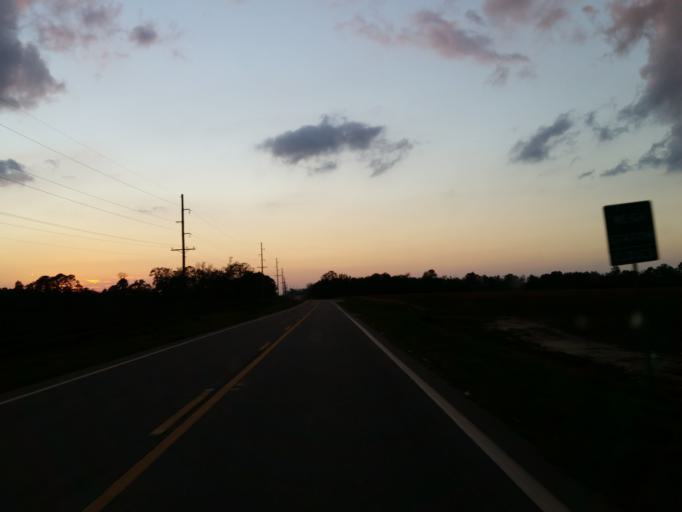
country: US
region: Georgia
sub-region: Dooly County
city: Vienna
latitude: 32.1236
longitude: -83.7276
